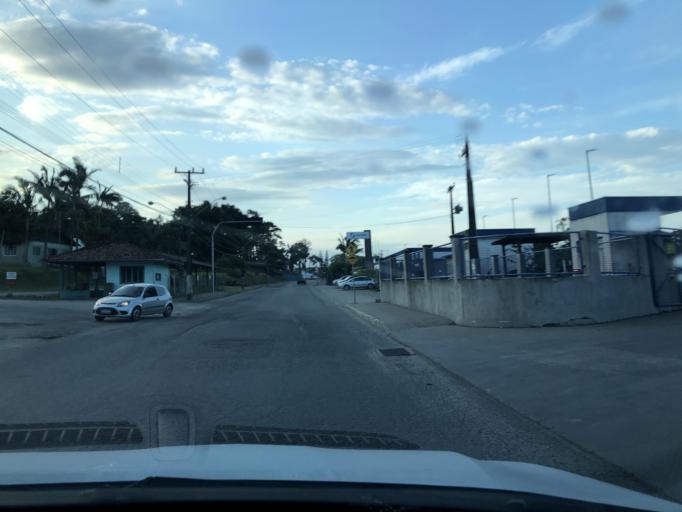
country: BR
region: Santa Catarina
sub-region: Sao Francisco Do Sul
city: Sao Francisco do Sul
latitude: -26.2575
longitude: -48.6235
